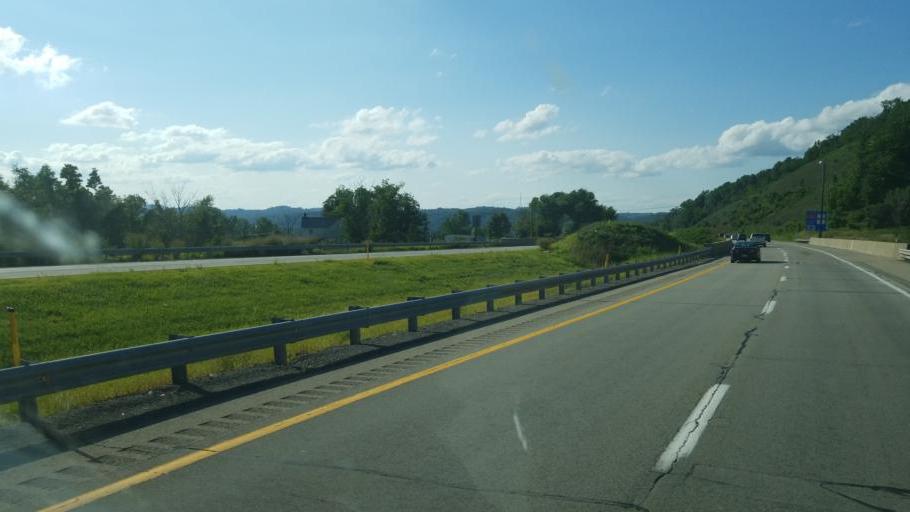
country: US
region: Pennsylvania
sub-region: Greene County
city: Morrisville
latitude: 39.8892
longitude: -80.1340
